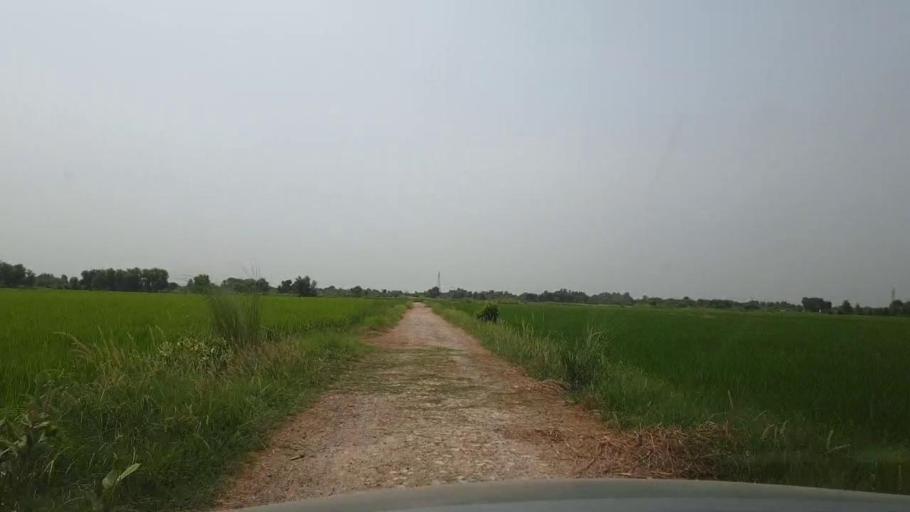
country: PK
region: Sindh
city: Madeji
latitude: 27.7920
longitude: 68.5378
